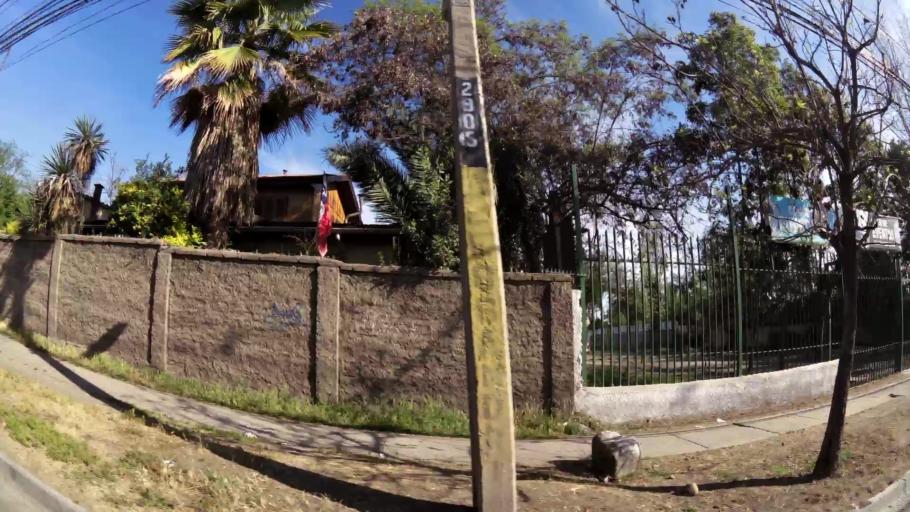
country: CL
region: Santiago Metropolitan
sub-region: Provincia de Santiago
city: Villa Presidente Frei, Nunoa, Santiago, Chile
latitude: -33.5120
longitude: -70.5577
